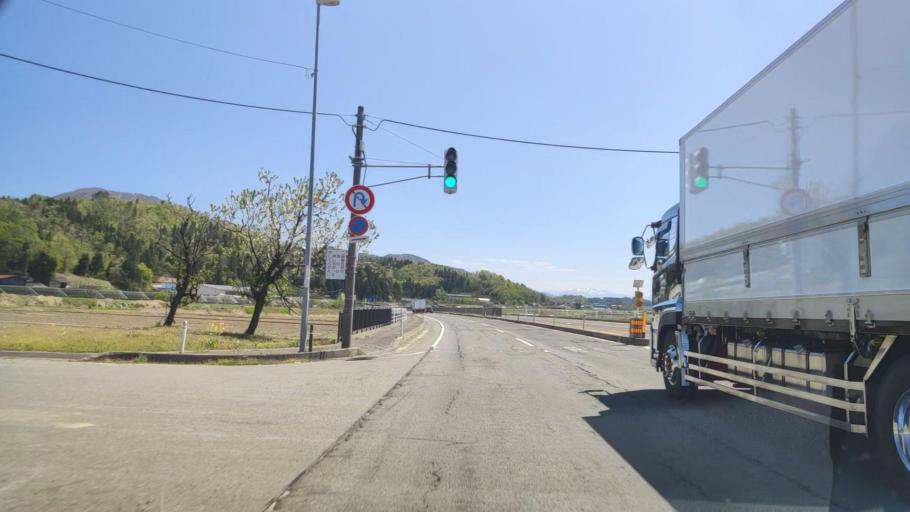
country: JP
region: Yamagata
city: Obanazawa
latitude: 38.5306
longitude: 140.3932
